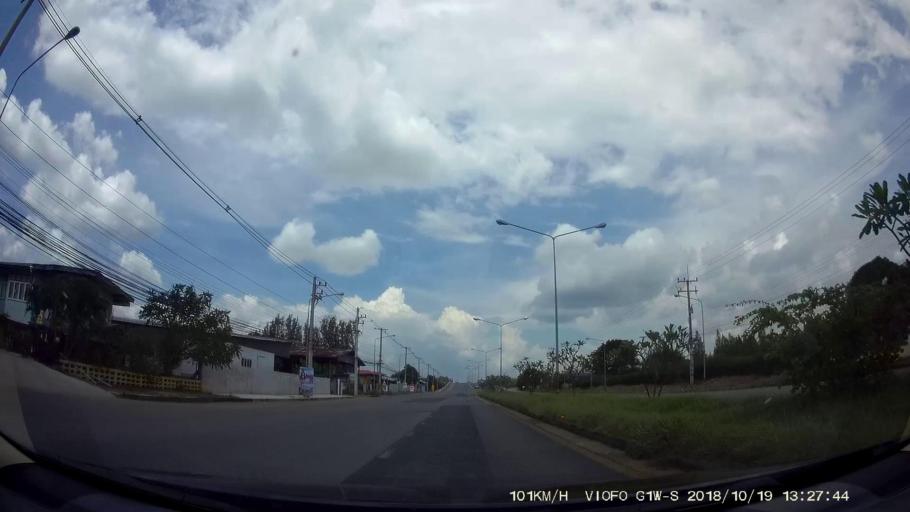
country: TH
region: Chaiyaphum
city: Chatturat
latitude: 15.5524
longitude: 101.8432
